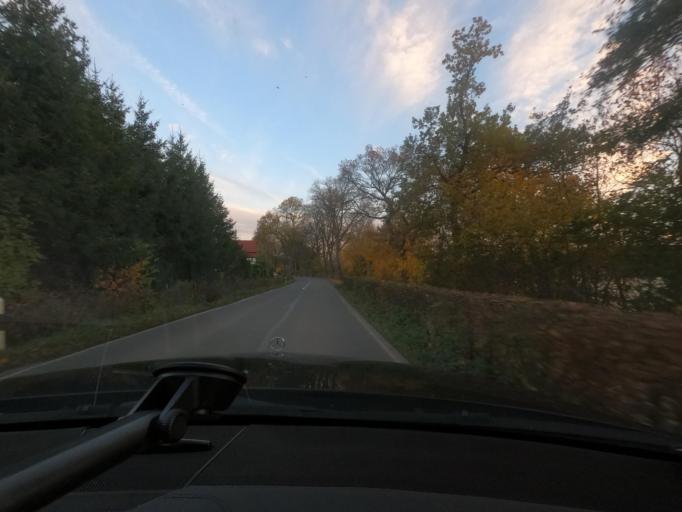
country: DE
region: North Rhine-Westphalia
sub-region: Regierungsbezirk Arnsberg
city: Mohnesee
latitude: 51.4933
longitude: 8.1521
